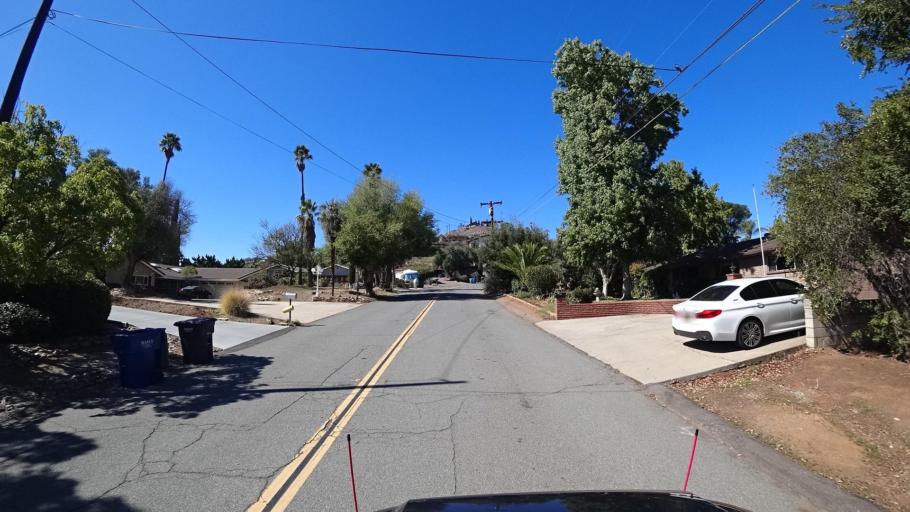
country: US
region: California
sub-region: San Diego County
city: Bostonia
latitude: 32.8188
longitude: -116.9376
